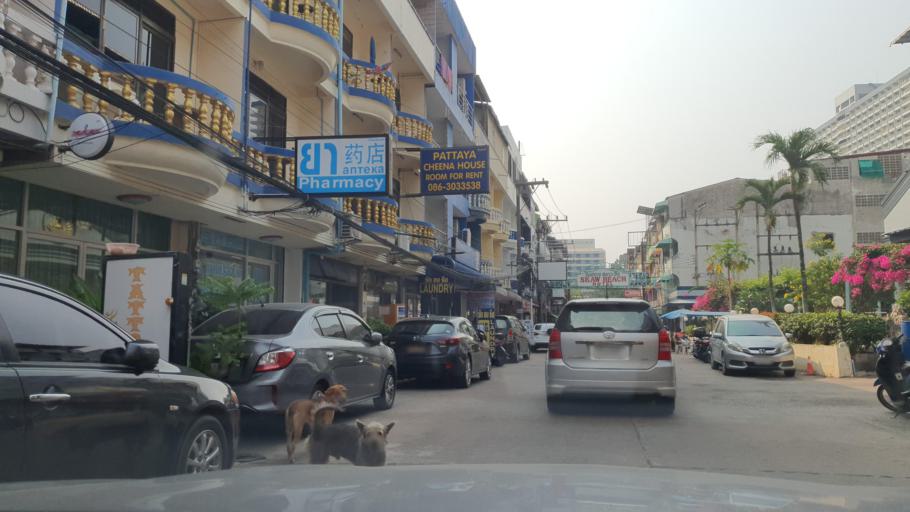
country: TH
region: Chon Buri
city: Phatthaya
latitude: 12.9313
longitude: 100.8847
